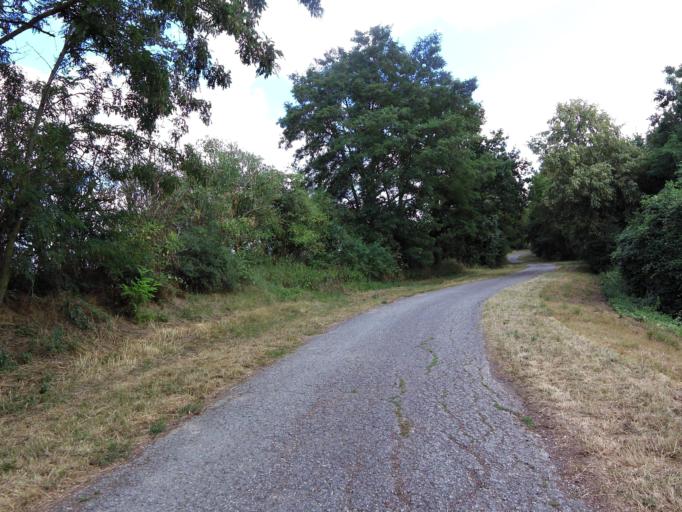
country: DE
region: Bavaria
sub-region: Regierungsbezirk Unterfranken
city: Gerbrunn
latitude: 49.7787
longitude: 10.0025
